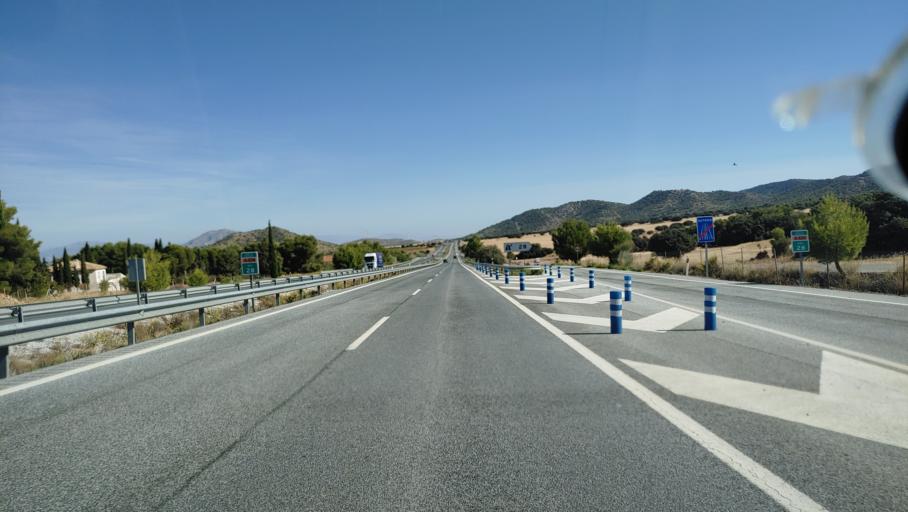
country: ES
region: Andalusia
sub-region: Provincia de Granada
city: Freila
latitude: 37.4427
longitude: -2.8935
